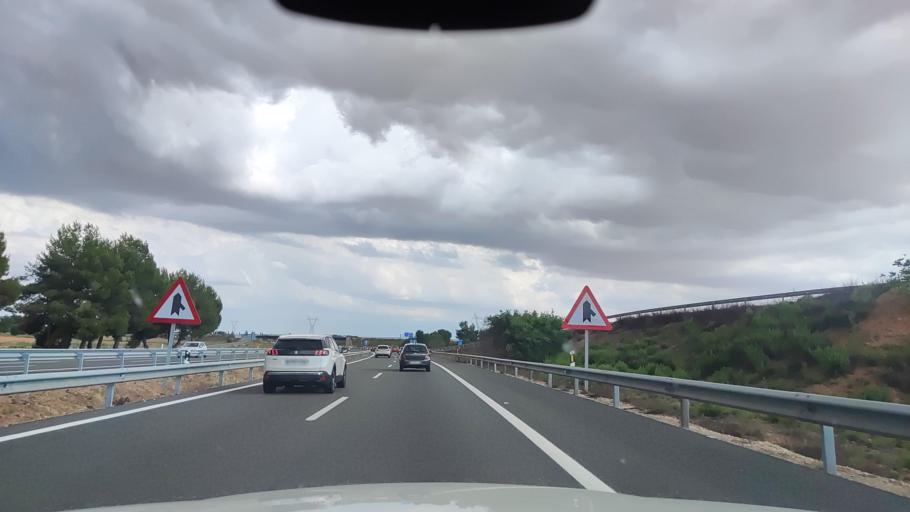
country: ES
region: Castille-La Mancha
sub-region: Provincia de Cuenca
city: Tarancon
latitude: 40.0043
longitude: -3.0269
